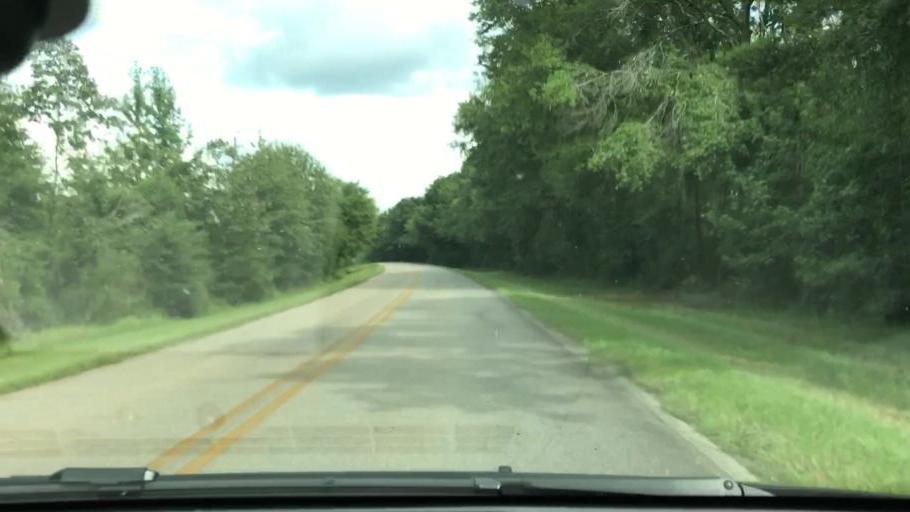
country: US
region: Georgia
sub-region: Clay County
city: Fort Gaines
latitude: 31.5725
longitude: -85.0140
